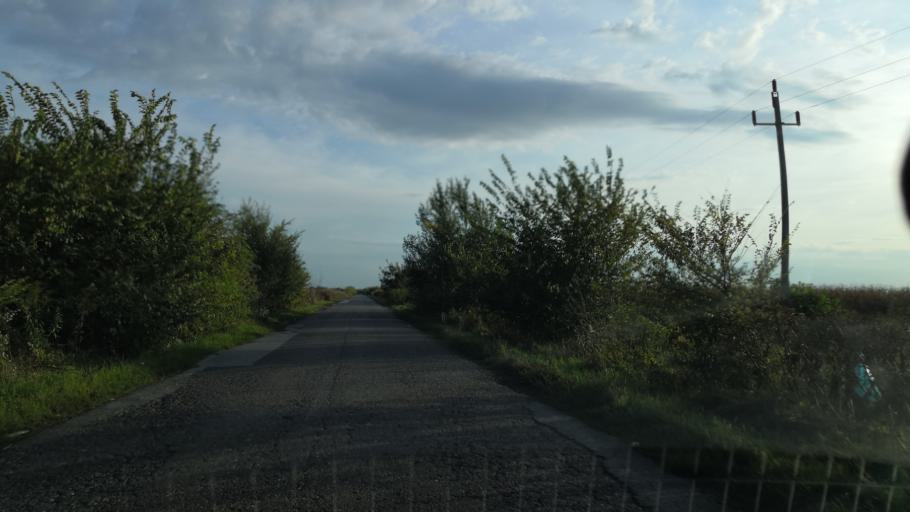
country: RS
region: Autonomna Pokrajina Vojvodina
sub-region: Sremski Okrug
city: Stara Pazova
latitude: 45.0068
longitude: 20.1665
